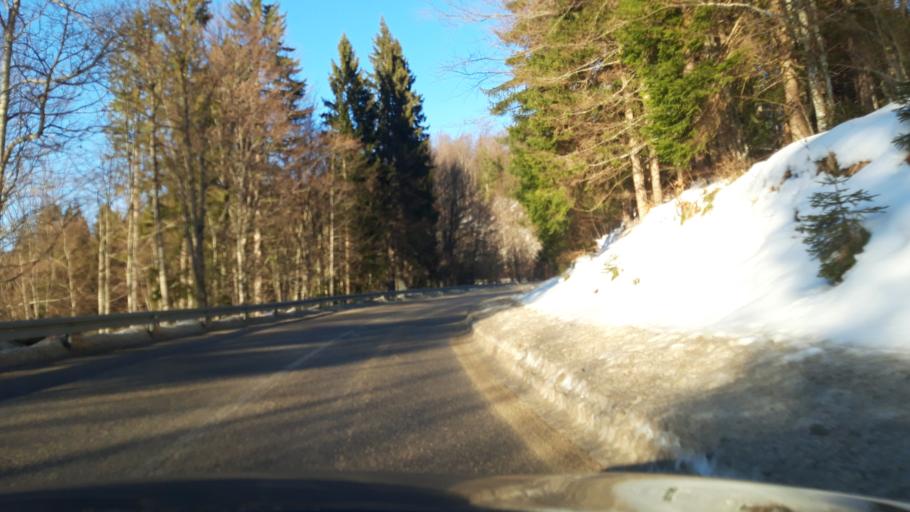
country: BA
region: Republika Srpska
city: Han Pijesak
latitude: 44.1322
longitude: 18.9549
